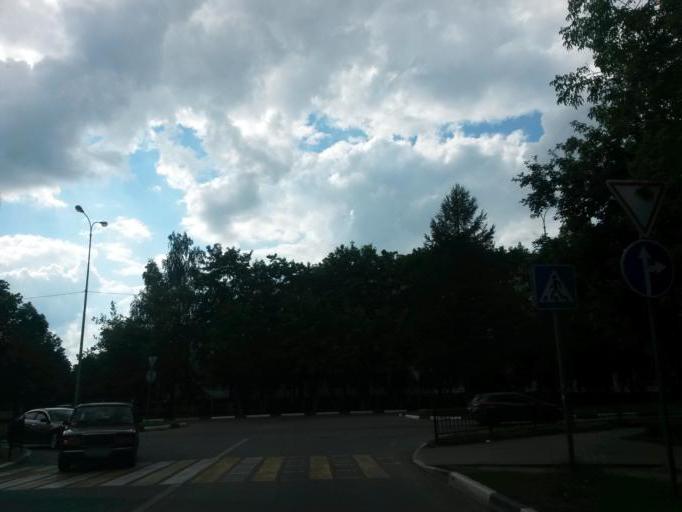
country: RU
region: Moskovskaya
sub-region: Chekhovskiy Rayon
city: Chekhov
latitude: 55.1518
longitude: 37.4685
